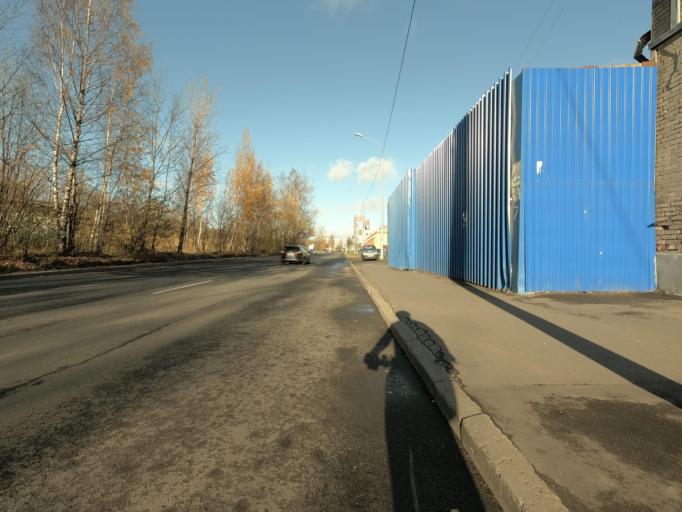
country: RU
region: St.-Petersburg
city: Krasnogvargeisky
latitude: 59.9502
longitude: 30.4478
